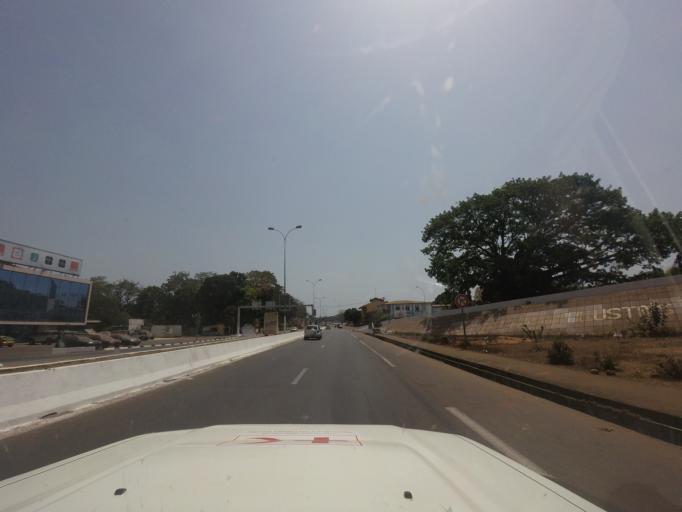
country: GN
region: Conakry
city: Camayenne
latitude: 9.5249
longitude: -13.6887
